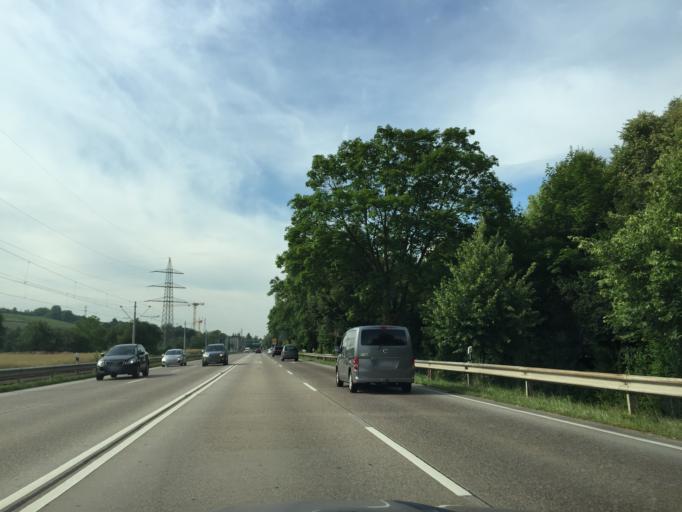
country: DE
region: Baden-Wuerttemberg
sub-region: Karlsruhe Region
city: Leimen
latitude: 49.3627
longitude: 8.6887
